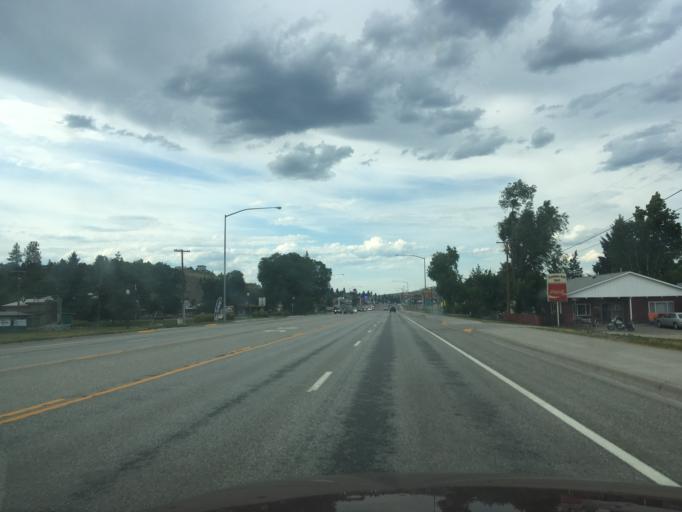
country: US
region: Montana
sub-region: Missoula County
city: Lolo
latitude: 46.7523
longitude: -114.0827
